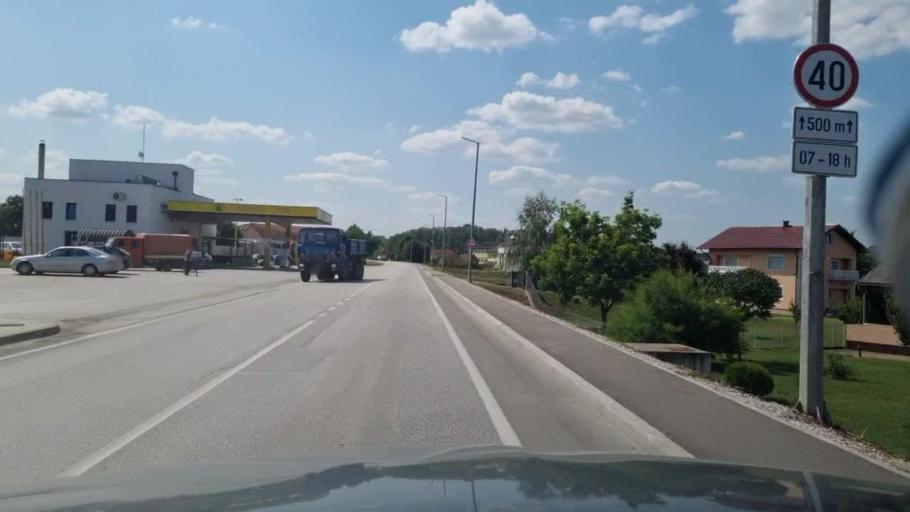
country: BA
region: Republika Srpska
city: Ostra Luka
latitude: 45.0628
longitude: 18.5803
